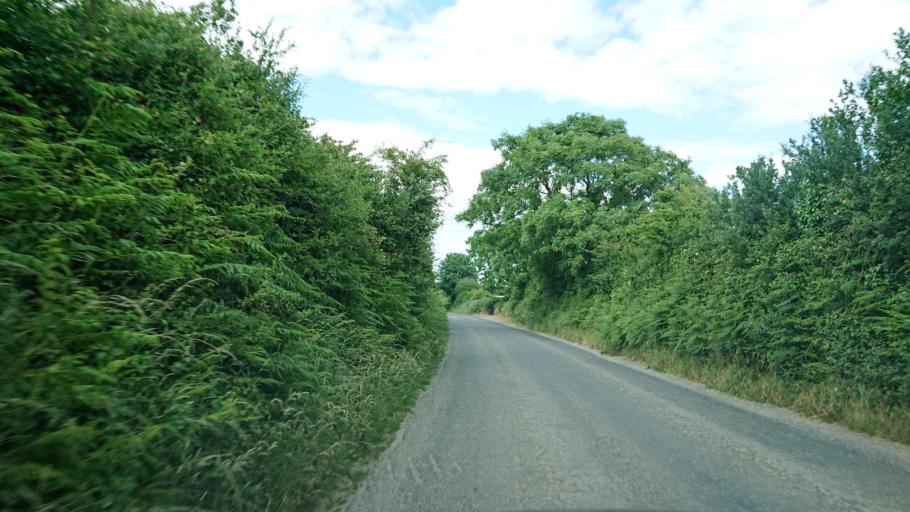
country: IE
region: Munster
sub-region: Waterford
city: Waterford
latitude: 52.2224
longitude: -7.1537
